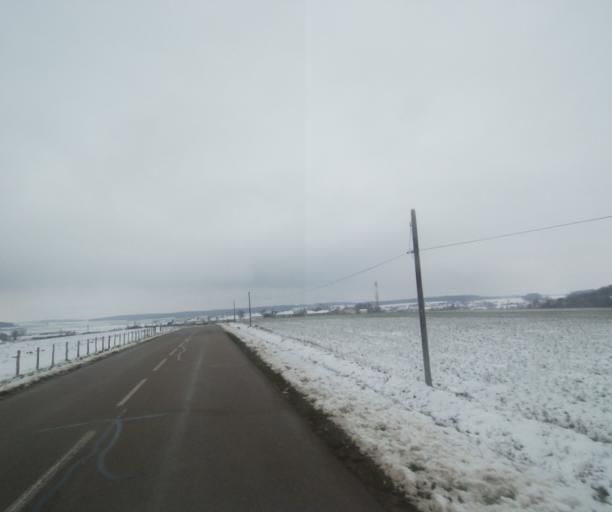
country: FR
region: Champagne-Ardenne
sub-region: Departement de la Haute-Marne
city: Laneuville-a-Remy
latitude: 48.4223
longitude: 4.8406
